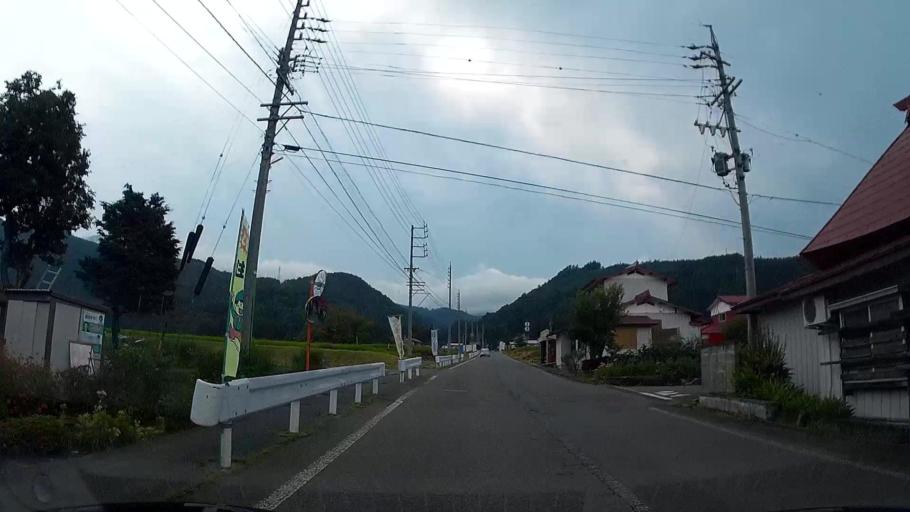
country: JP
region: Nagano
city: Iiyama
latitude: 36.8301
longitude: 138.4156
